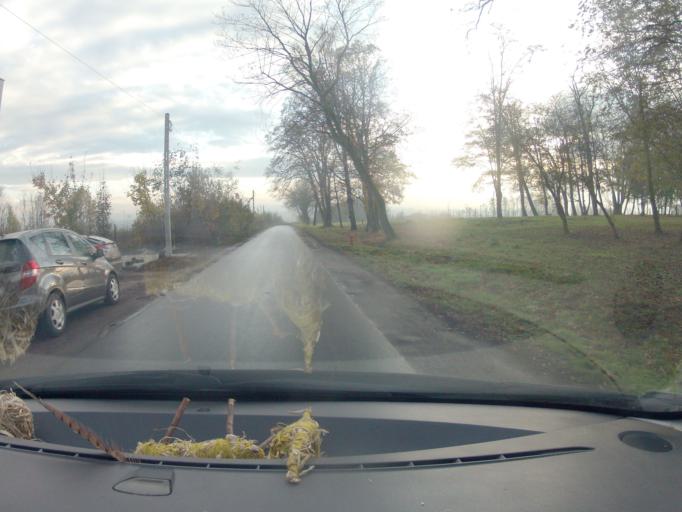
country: PL
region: Lesser Poland Voivodeship
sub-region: Krakow
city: Sidzina
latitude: 50.0012
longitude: 19.8873
